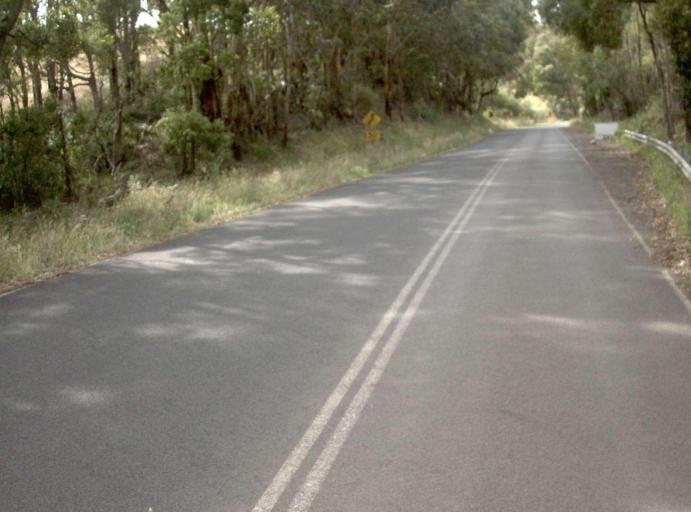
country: AU
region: Victoria
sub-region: Latrobe
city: Moe
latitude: -38.2340
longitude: 146.1685
